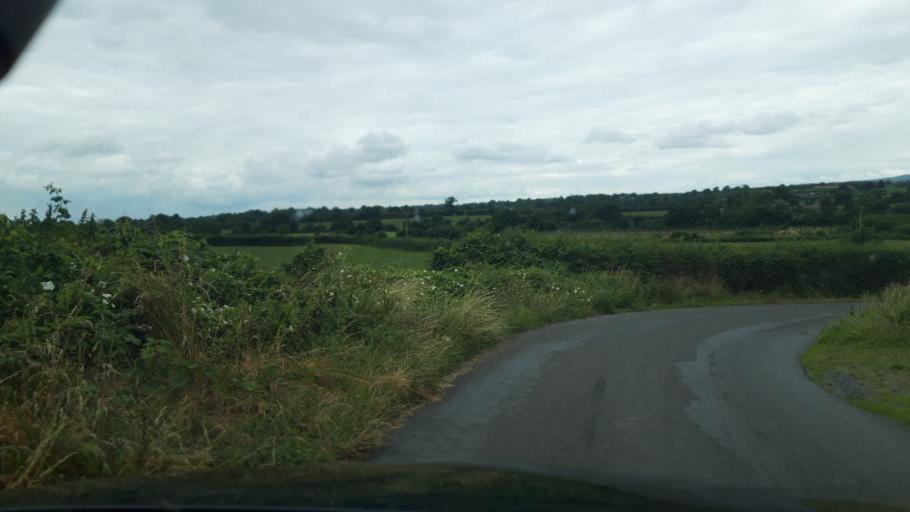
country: IE
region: Leinster
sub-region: Kilkenny
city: Graiguenamanagh
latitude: 52.5924
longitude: -7.0286
